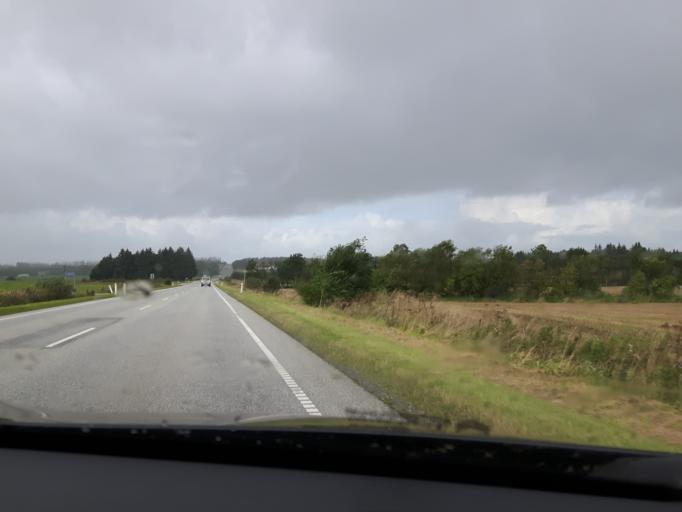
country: DK
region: North Denmark
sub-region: Jammerbugt Kommune
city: Fjerritslev
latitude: 57.0879
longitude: 9.3291
